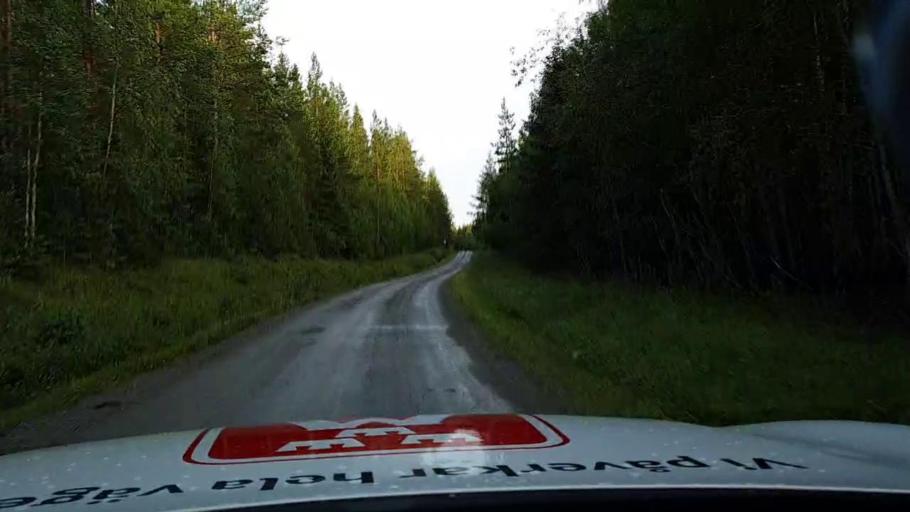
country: SE
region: Jaemtland
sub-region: Bergs Kommun
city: Hoverberg
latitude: 62.8609
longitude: 14.5326
